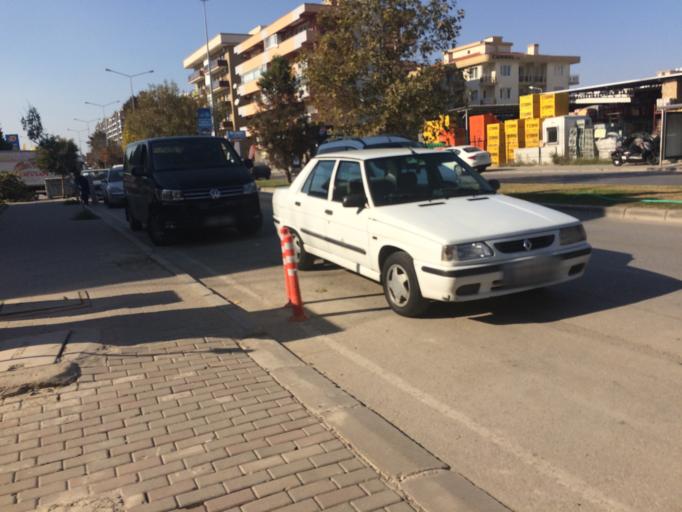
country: TR
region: Izmir
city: Karsiyaka
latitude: 38.4933
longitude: 27.0532
